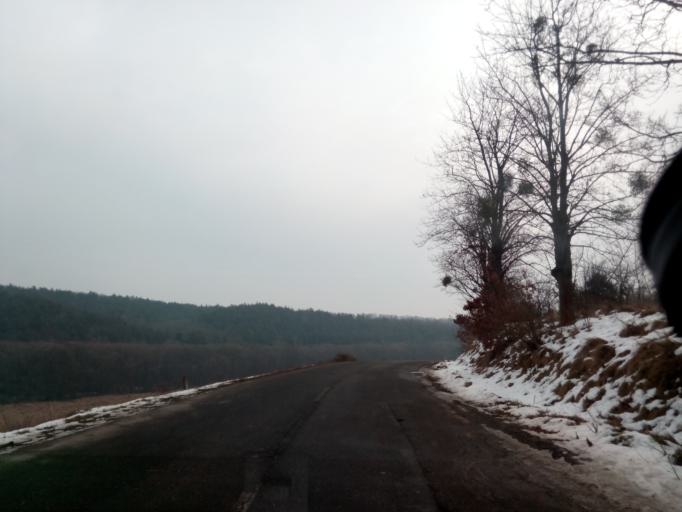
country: HU
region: Borsod-Abauj-Zemplen
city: Gonc
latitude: 48.5020
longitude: 21.3380
